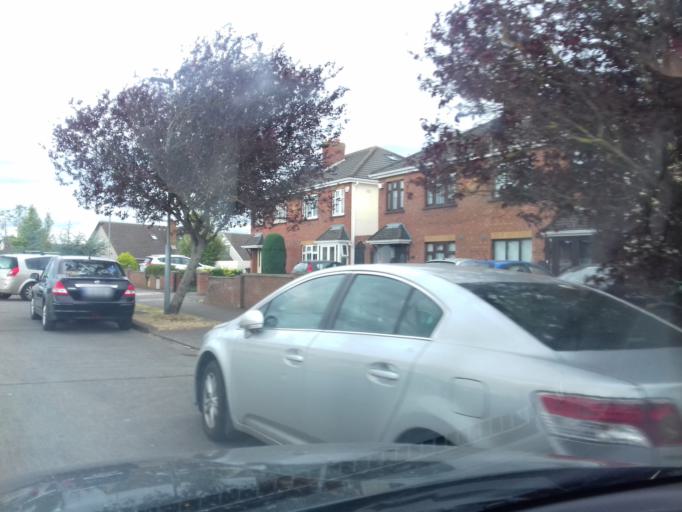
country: IE
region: Leinster
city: Hartstown
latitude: 53.3900
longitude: -6.4197
